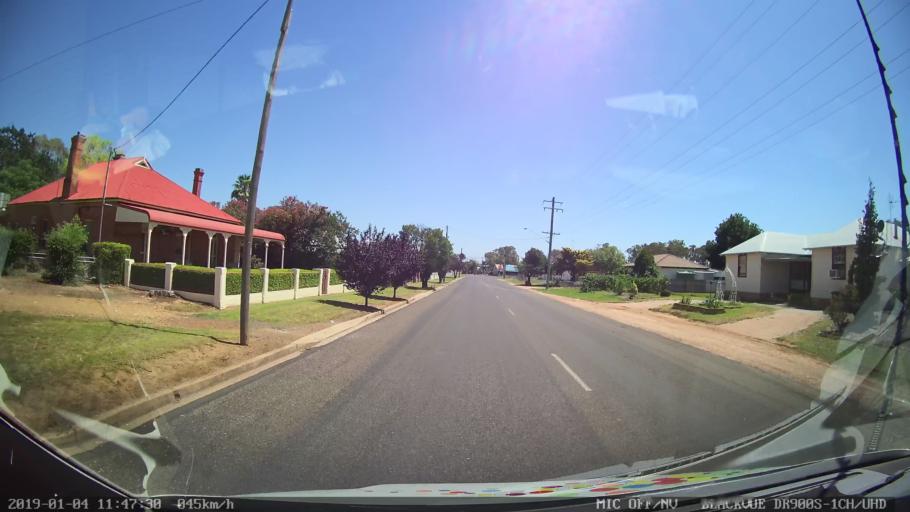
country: AU
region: New South Wales
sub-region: Cabonne
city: Molong
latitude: -32.9324
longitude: 148.7549
